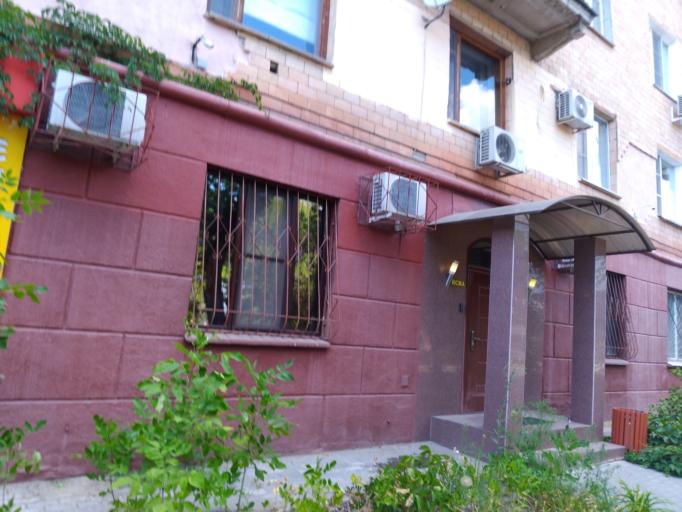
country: RU
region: Volgograd
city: Volgograd
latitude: 48.7135
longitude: 44.5320
